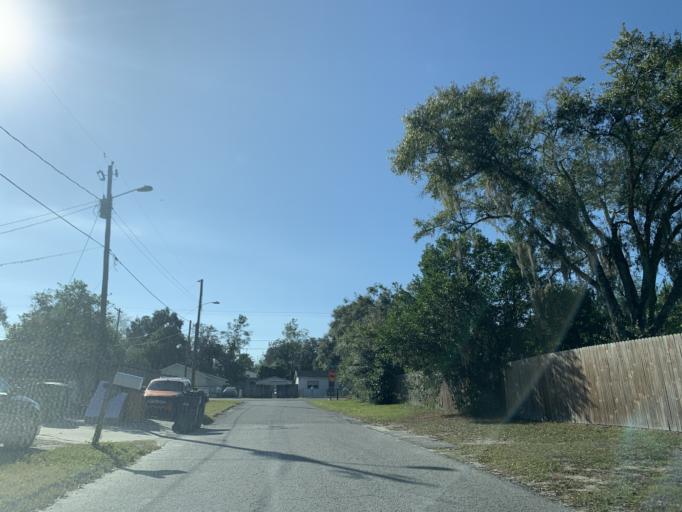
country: US
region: Florida
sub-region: Hillsborough County
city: Temple Terrace
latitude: 28.0258
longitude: -82.4119
